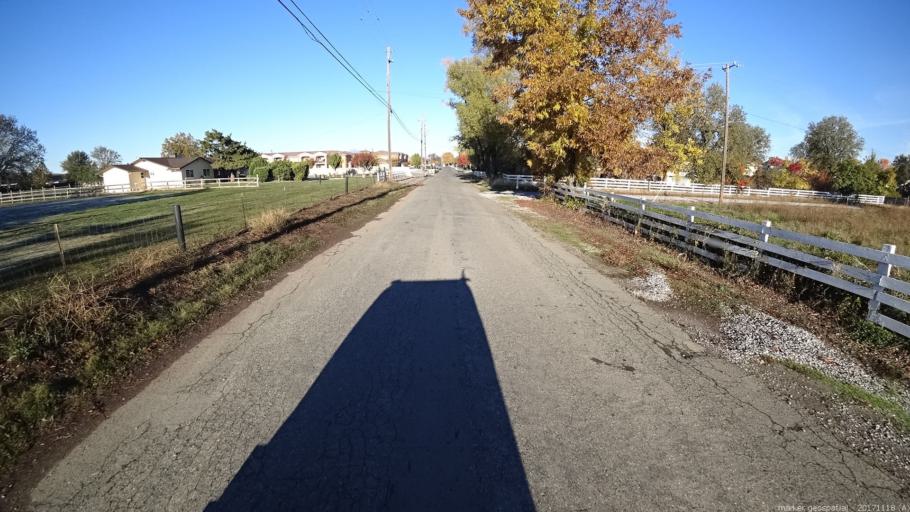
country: US
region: California
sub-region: Shasta County
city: Anderson
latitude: 40.4514
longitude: -122.2824
